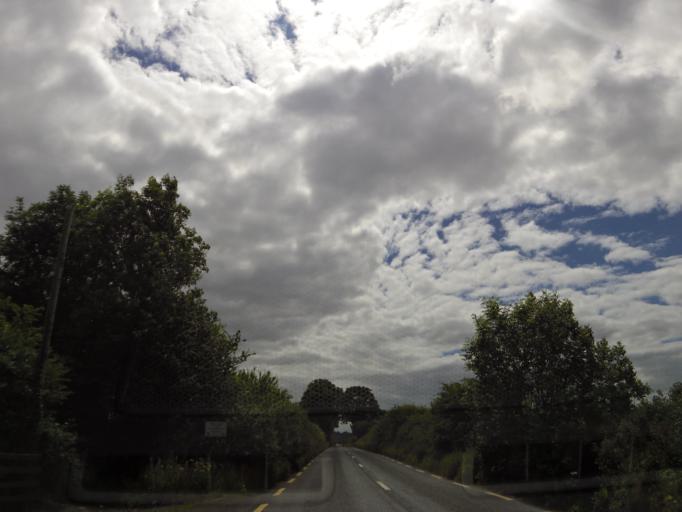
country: IE
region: Munster
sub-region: North Tipperary
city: Nenagh
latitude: 52.7900
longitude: -8.0371
